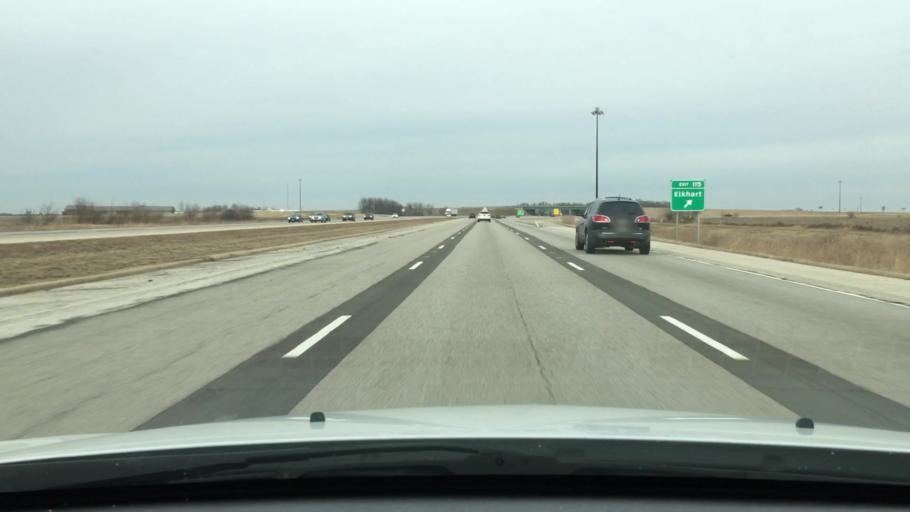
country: US
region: Illinois
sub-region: Sangamon County
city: Williamsville
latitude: 40.0141
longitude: -89.4989
